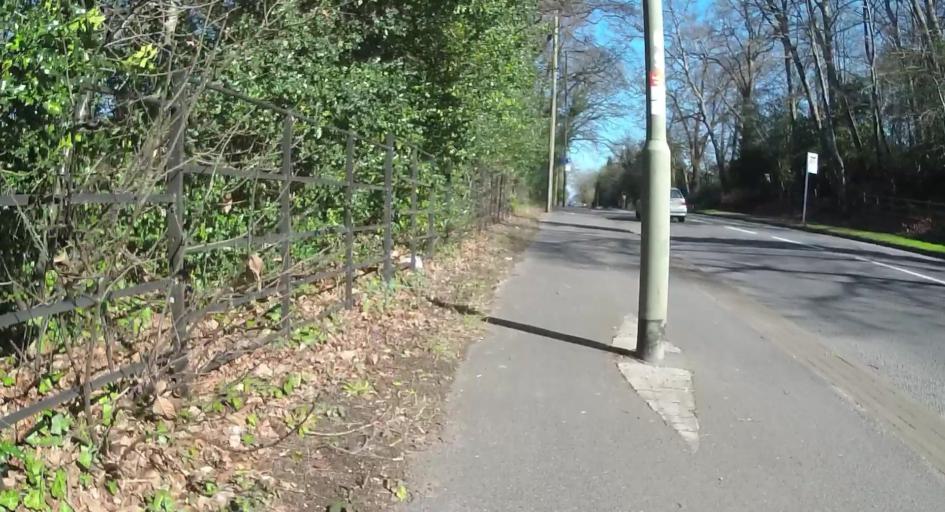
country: GB
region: England
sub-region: Bracknell Forest
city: Bracknell
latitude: 51.4129
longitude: -0.7275
